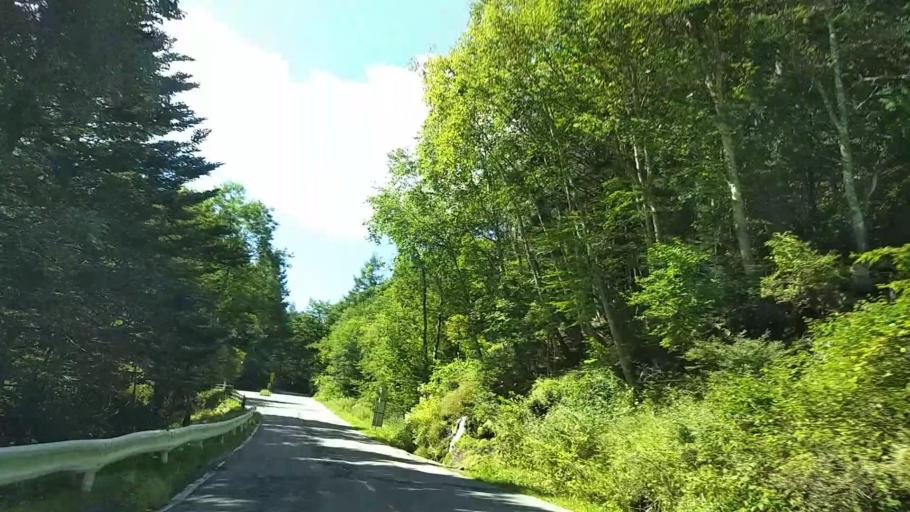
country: JP
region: Nagano
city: Chino
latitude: 36.0799
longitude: 138.2935
